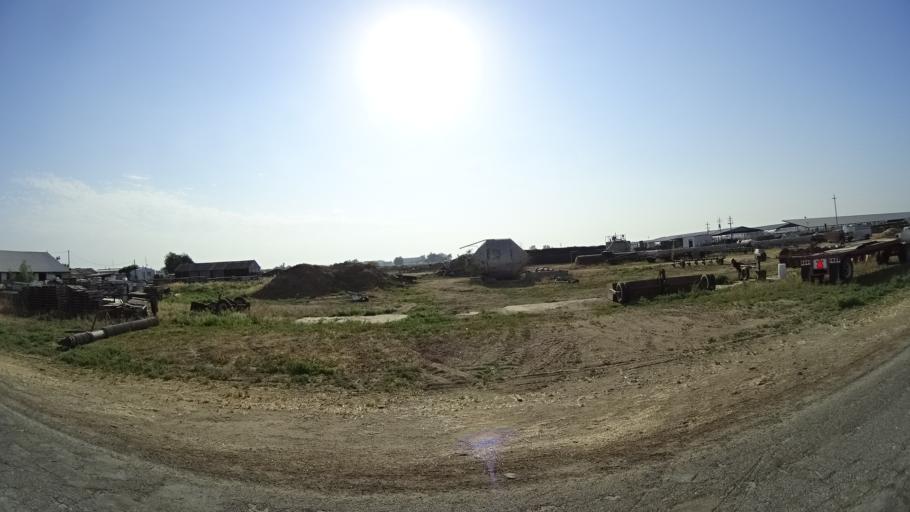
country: US
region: California
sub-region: Fresno County
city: Riverdale
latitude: 36.3777
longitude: -119.8431
